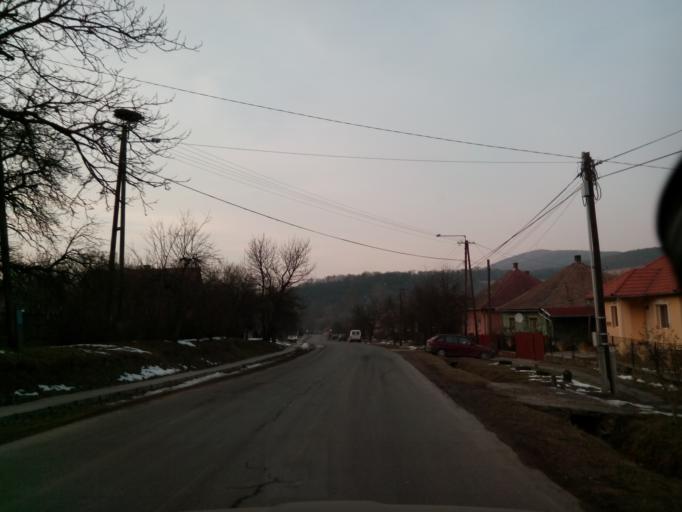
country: HU
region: Borsod-Abauj-Zemplen
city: Gonc
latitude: 48.4910
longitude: 21.3488
